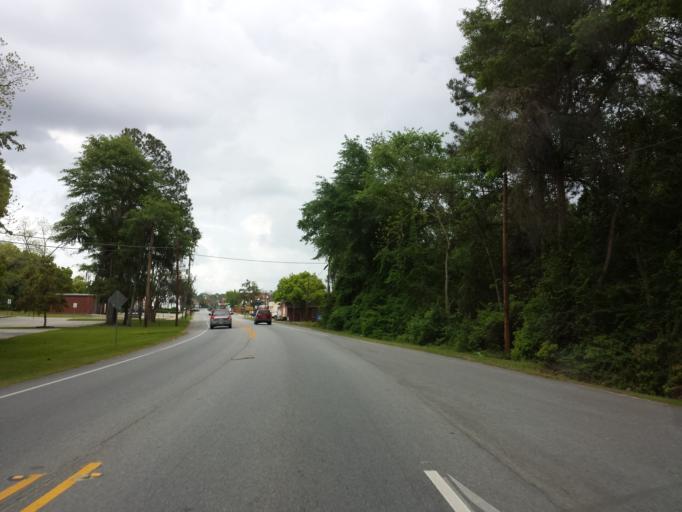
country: US
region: Georgia
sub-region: Lowndes County
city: Hahira
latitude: 30.9900
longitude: -83.3786
